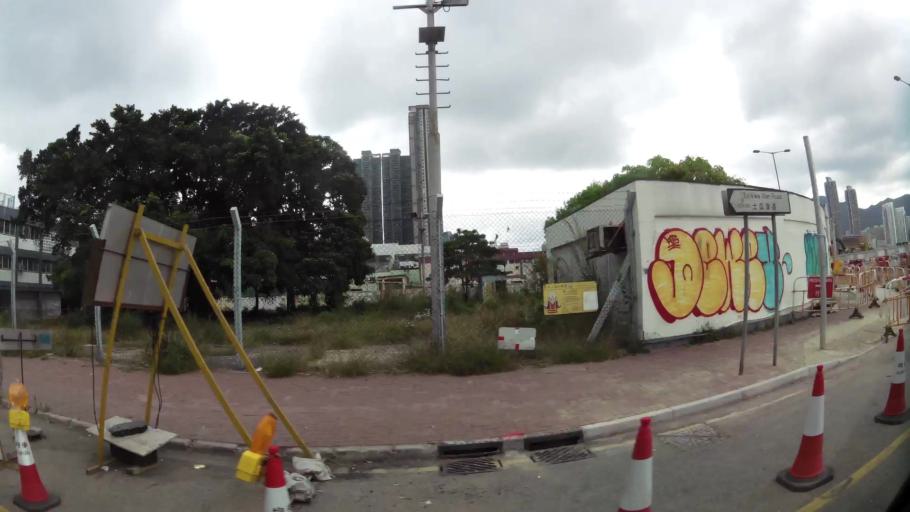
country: HK
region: Kowloon City
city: Kowloon
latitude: 22.3219
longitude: 114.1943
